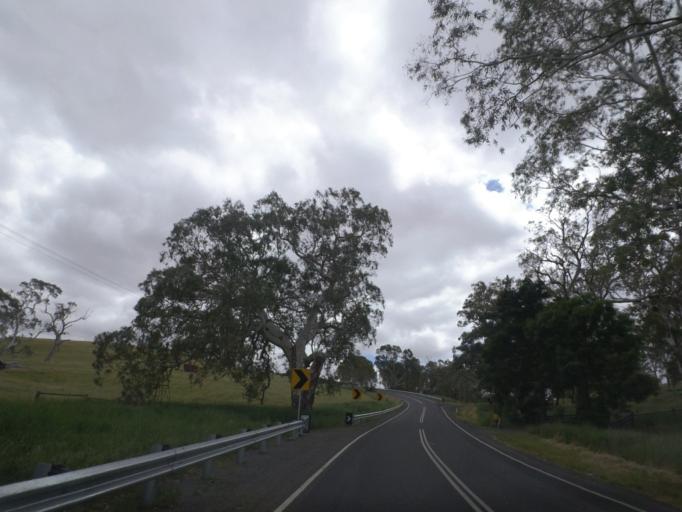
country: AU
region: Victoria
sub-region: Whittlesea
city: Whittlesea
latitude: -37.1908
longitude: 145.0386
